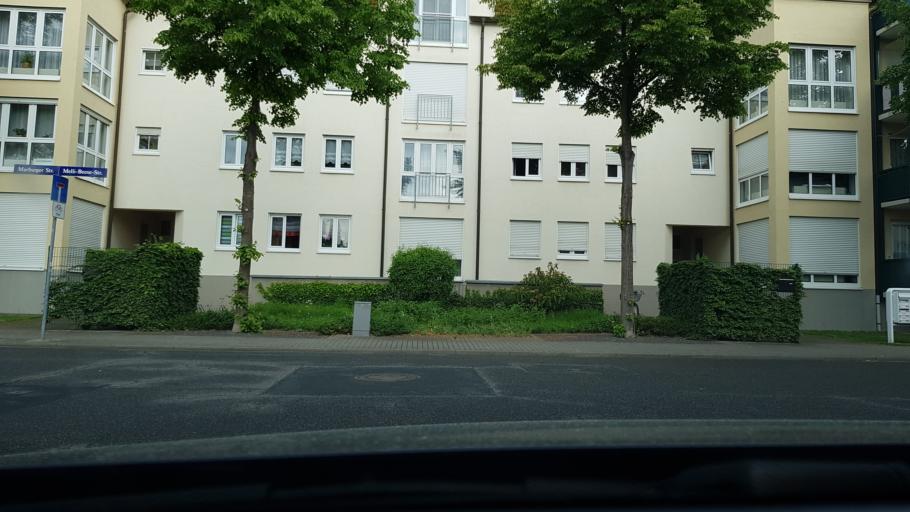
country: DE
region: Saxony
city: Heidenau
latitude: 51.0181
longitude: 13.8341
